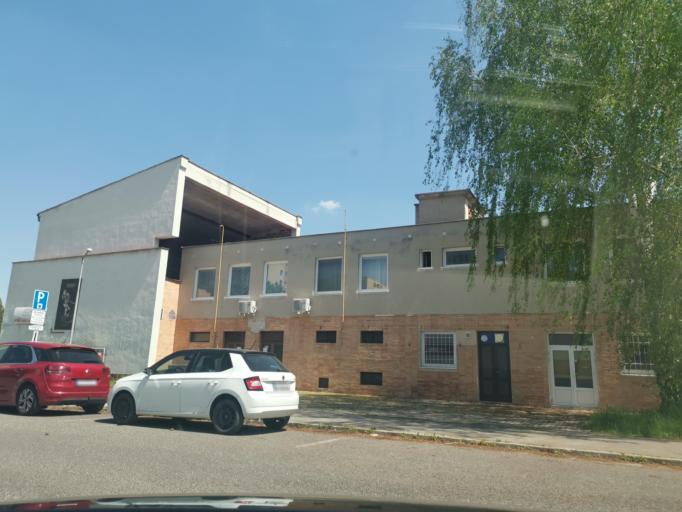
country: SK
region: Trnavsky
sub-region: Okres Senica
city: Senica
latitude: 48.6855
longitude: 17.3757
